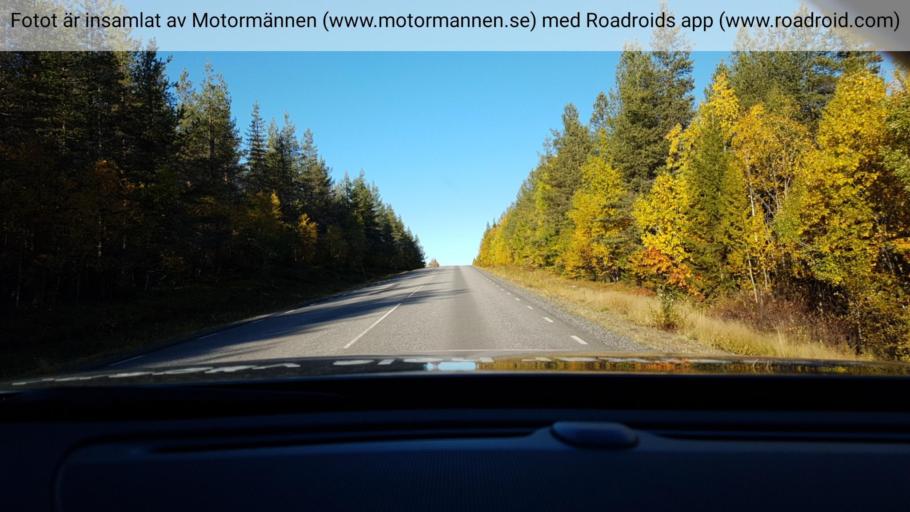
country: SE
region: Vaesterbotten
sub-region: Skelleftea Kommun
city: Storvik
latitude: 65.3248
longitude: 20.7637
